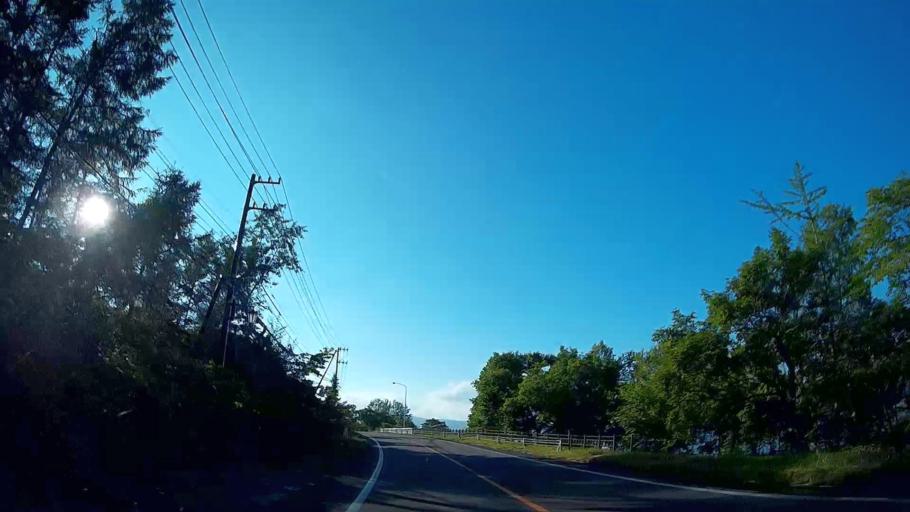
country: JP
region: Hokkaido
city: Date
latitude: 42.5613
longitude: 140.8477
